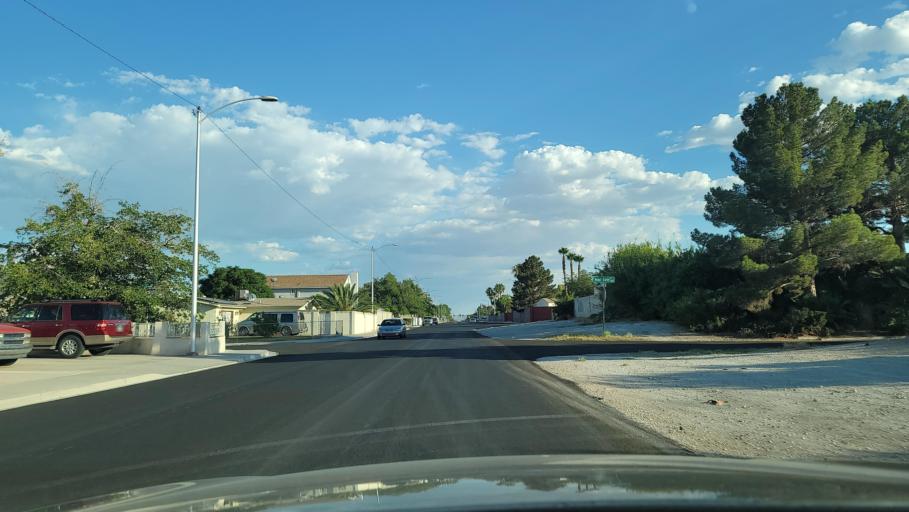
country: US
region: Nevada
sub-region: Clark County
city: Spring Valley
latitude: 36.1568
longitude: -115.2168
